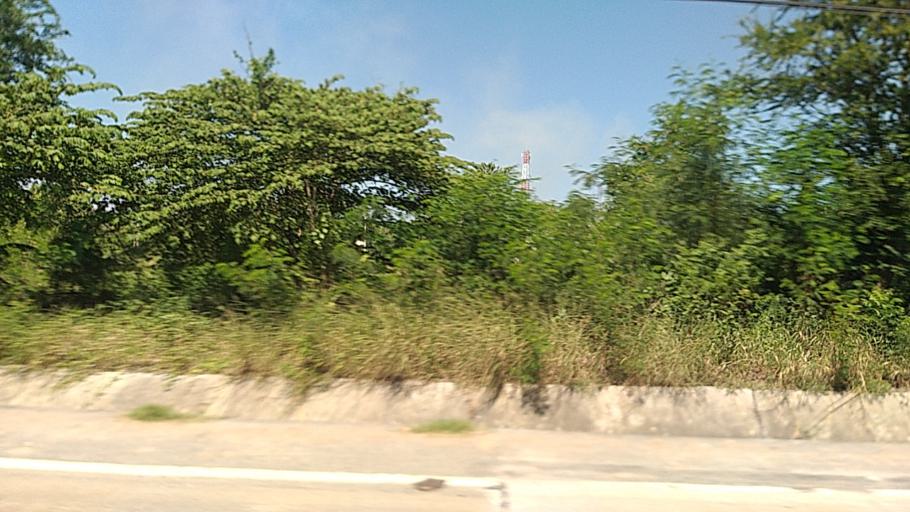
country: TH
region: Nakhon Ratchasima
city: Sikhio
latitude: 14.8698
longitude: 101.7268
